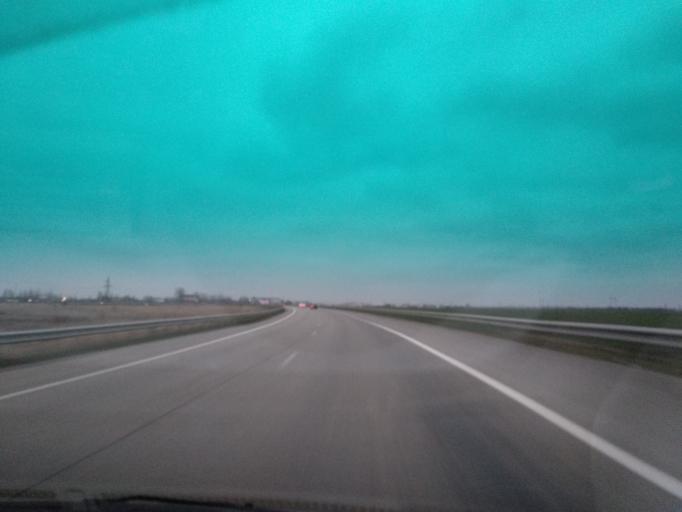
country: RU
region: Adygeya
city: Adygeysk
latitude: 44.8927
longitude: 39.1663
